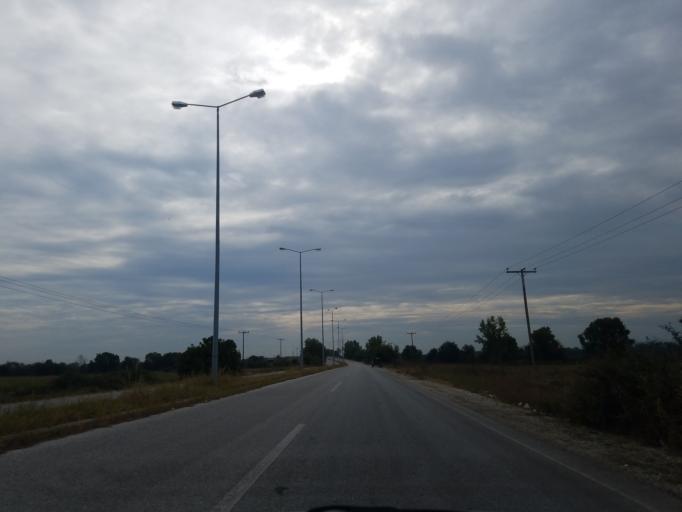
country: GR
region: Thessaly
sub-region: Trikala
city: Pyrgetos
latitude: 39.5240
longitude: 21.7510
